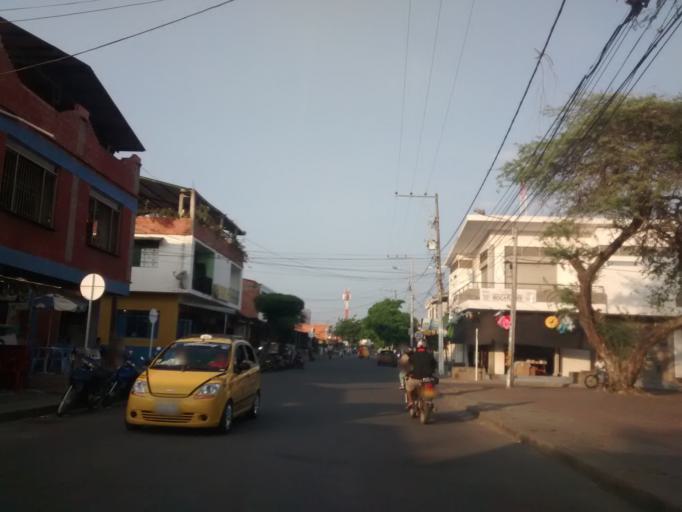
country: CO
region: Cundinamarca
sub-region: Girardot
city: Girardot City
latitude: 4.3135
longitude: -74.7880
